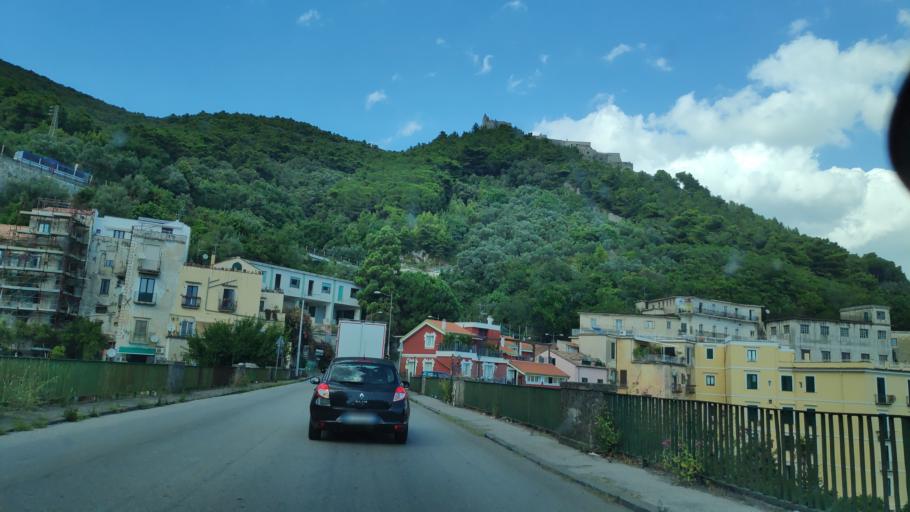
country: IT
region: Campania
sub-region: Provincia di Salerno
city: Vietri sul Mare
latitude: 40.6814
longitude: 14.7512
